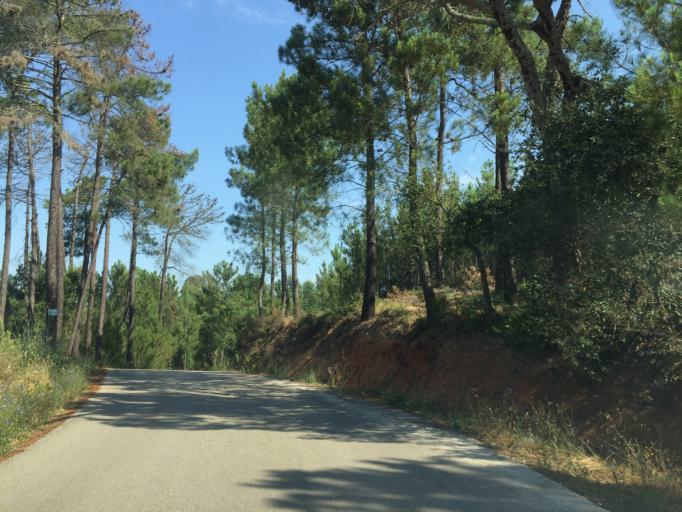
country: PT
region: Santarem
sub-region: Ferreira do Zezere
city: Ferreira do Zezere
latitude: 39.6020
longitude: -8.2936
